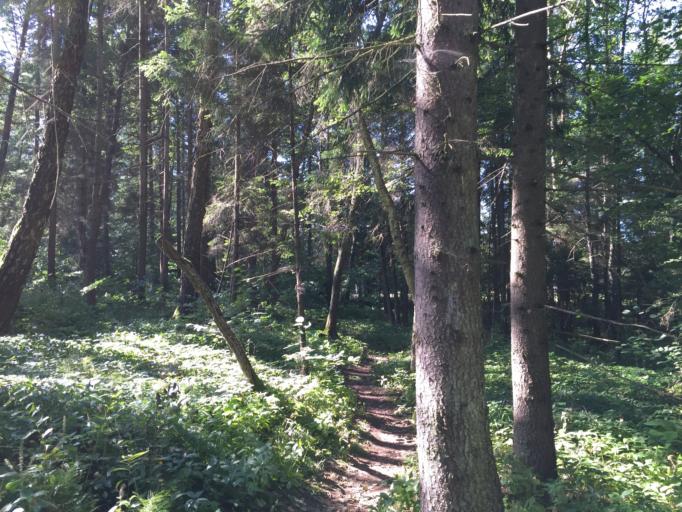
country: LT
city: Zarasai
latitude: 55.7920
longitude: 25.9617
